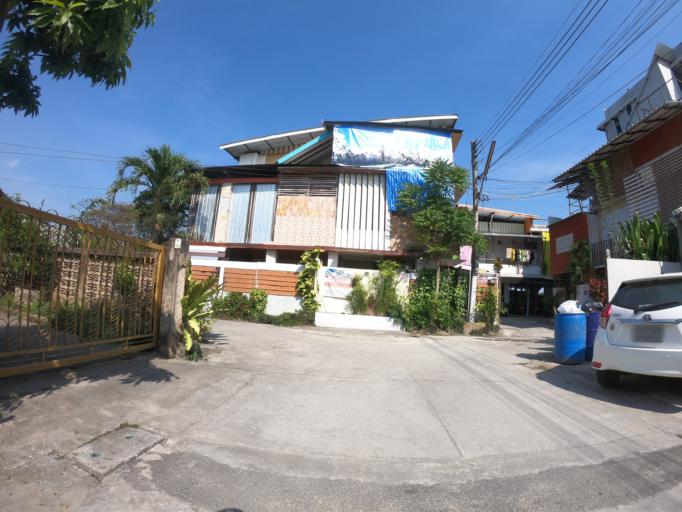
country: TH
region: Chiang Mai
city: Chiang Mai
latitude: 18.8148
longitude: 98.9883
